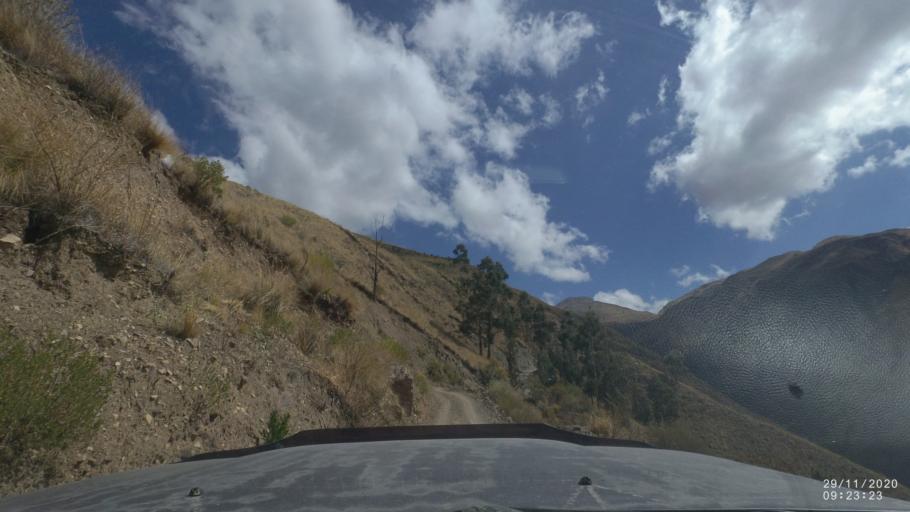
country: BO
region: Cochabamba
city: Cochabamba
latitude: -17.3214
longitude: -66.1859
